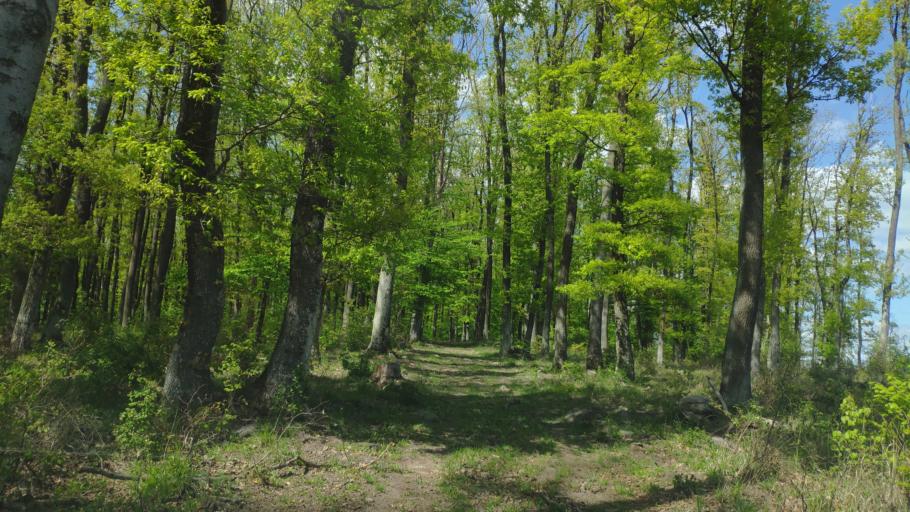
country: SK
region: Kosicky
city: Kosice
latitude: 48.6621
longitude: 21.4420
